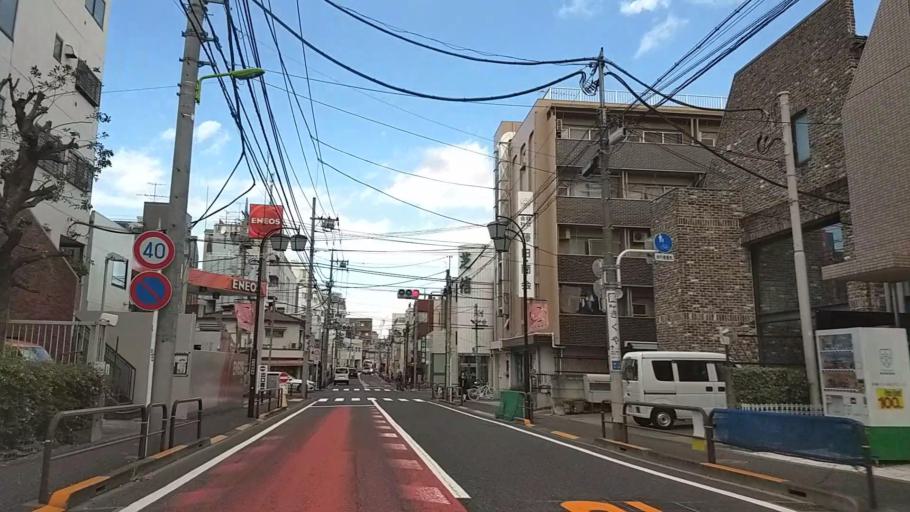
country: JP
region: Tokyo
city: Tokyo
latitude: 35.6535
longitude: 139.6672
